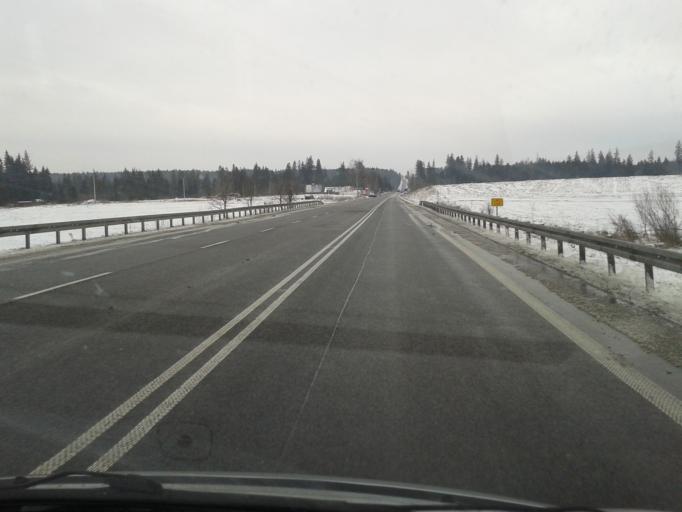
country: PL
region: Lesser Poland Voivodeship
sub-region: Powiat nowotarski
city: Chyzne
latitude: 49.3975
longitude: 19.6483
